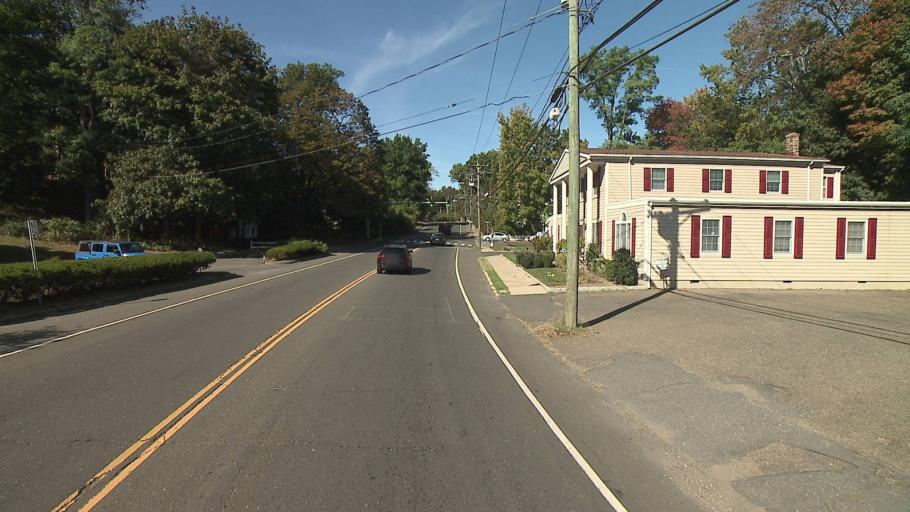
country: US
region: Connecticut
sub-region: Fairfield County
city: Darien
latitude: 41.0733
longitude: -73.4485
